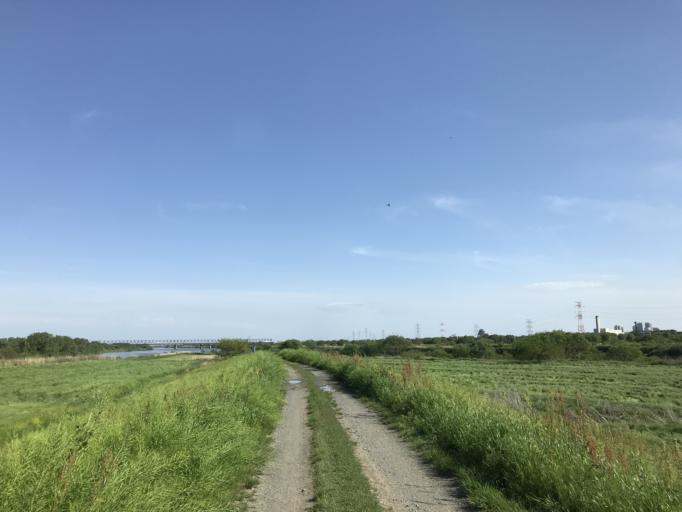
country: JP
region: Ibaraki
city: Moriya
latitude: 35.9410
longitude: 139.9451
